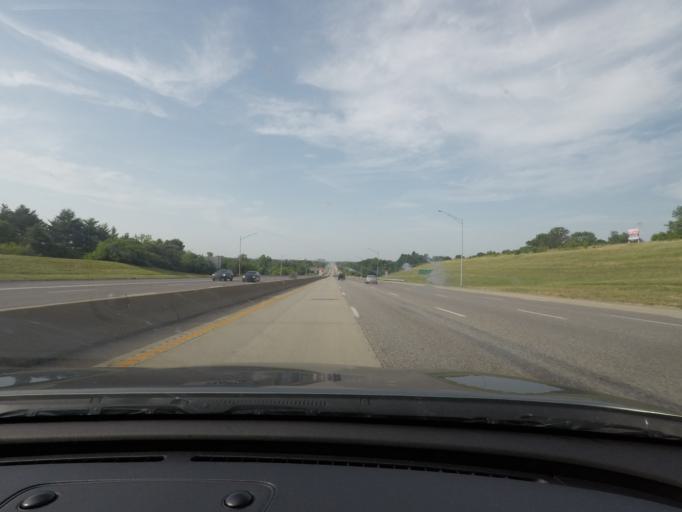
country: US
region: Missouri
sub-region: Saint Louis County
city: Maryland Heights
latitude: 38.7405
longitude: -90.4415
